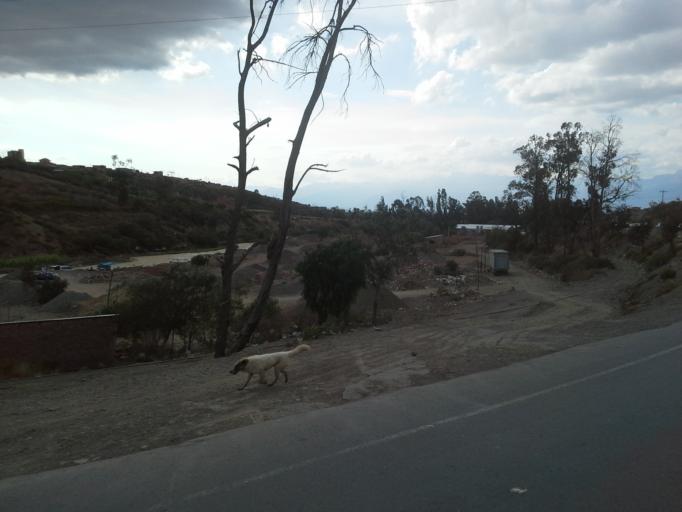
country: BO
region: Cochabamba
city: Cochabamba
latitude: -17.4715
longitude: -66.1128
